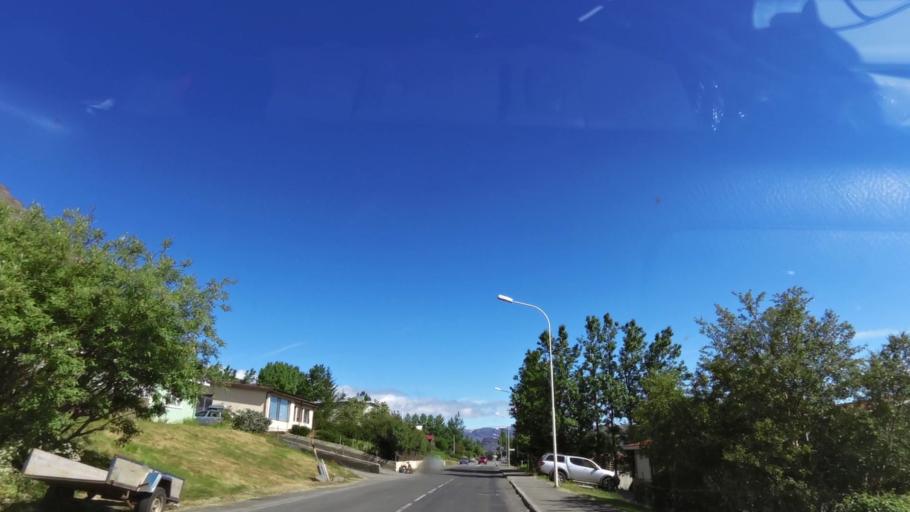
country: IS
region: Westfjords
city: Isafjoerdur
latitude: 65.6830
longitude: -23.6074
